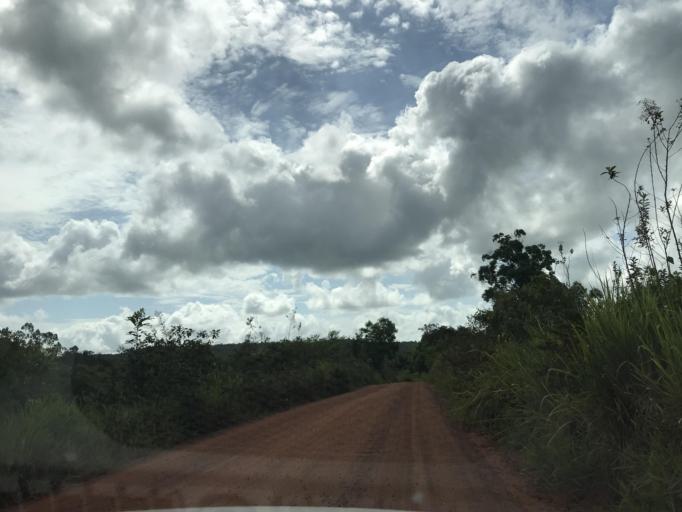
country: BR
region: Bahia
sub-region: Entre Rios
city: Entre Rios
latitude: -12.1771
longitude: -38.1273
